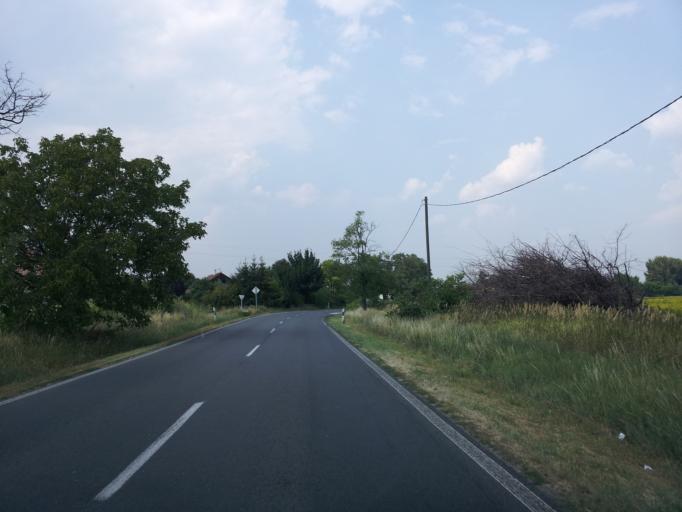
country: HU
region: Gyor-Moson-Sopron
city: Nyul
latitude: 47.5760
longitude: 17.6973
